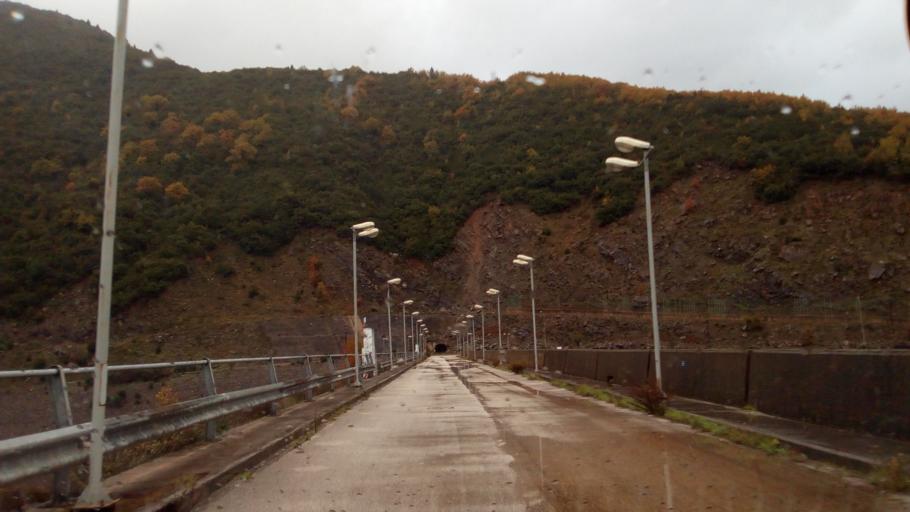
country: GR
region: West Greece
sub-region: Nomos Aitolias kai Akarnanias
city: Thermo
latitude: 38.6700
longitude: 21.8374
